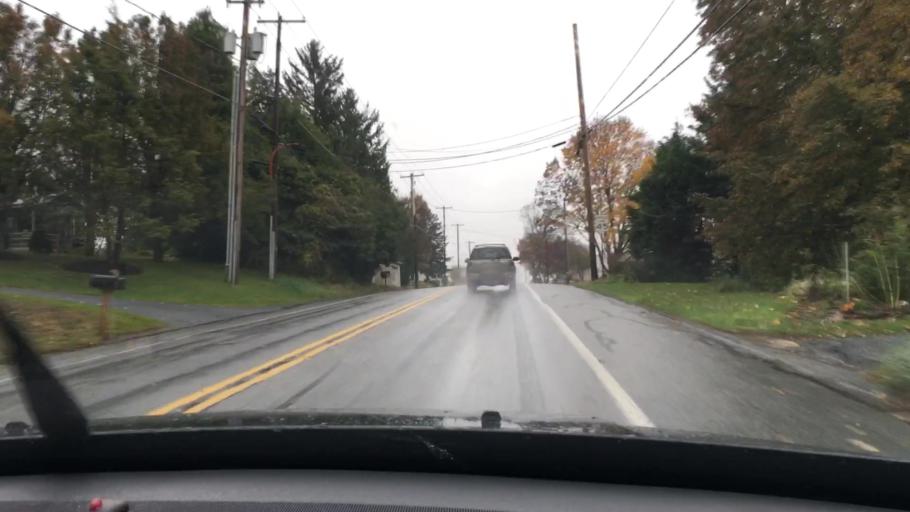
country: US
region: Pennsylvania
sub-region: Lancaster County
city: Quarryville
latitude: 39.8962
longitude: -76.2404
